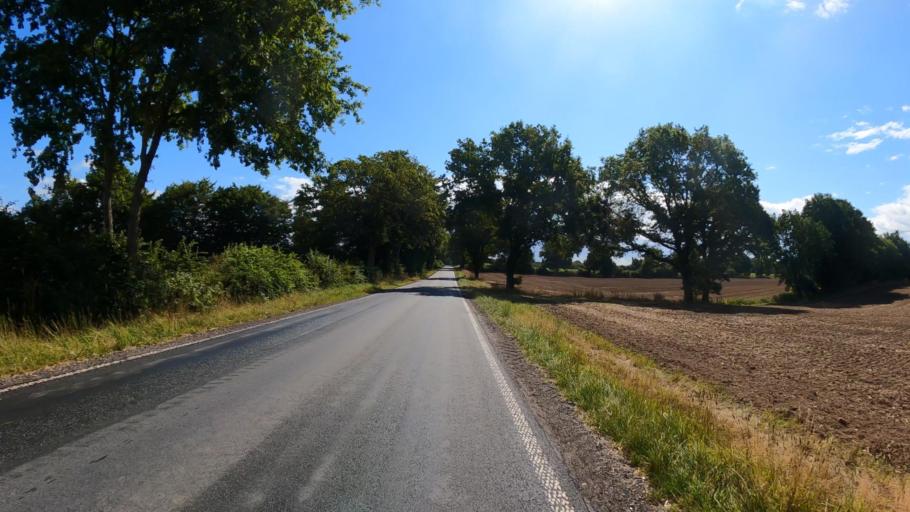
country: DE
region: Schleswig-Holstein
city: Armstedt
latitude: 53.9610
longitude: 9.8577
